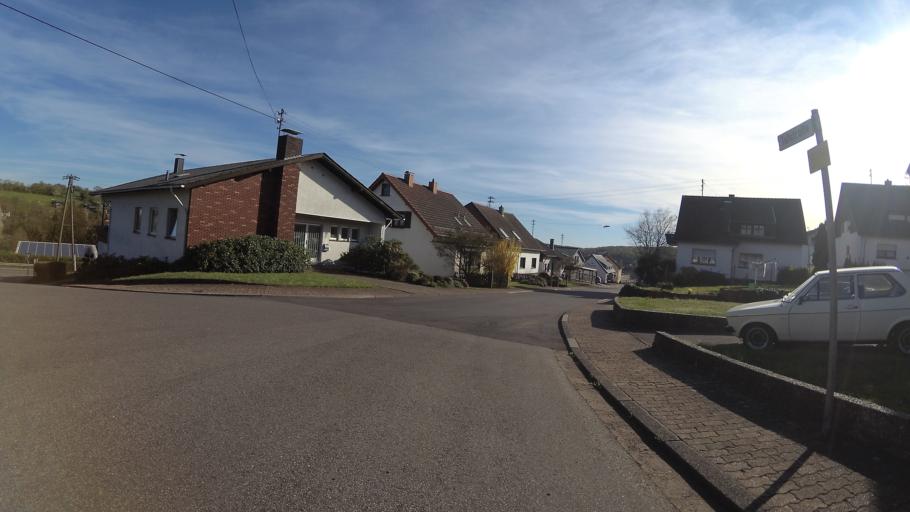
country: DE
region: Saarland
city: Marpingen
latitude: 49.4315
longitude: 7.0860
